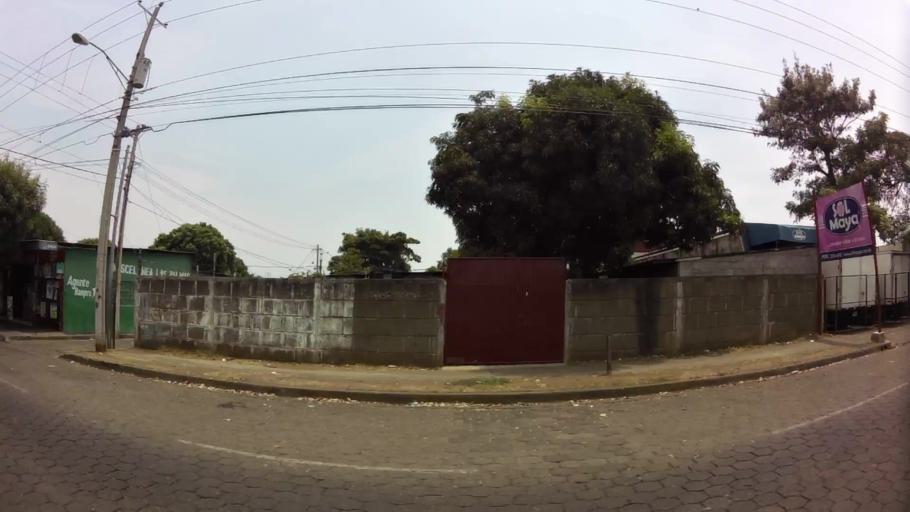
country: NI
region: Managua
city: Managua
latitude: 12.1450
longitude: -86.2947
